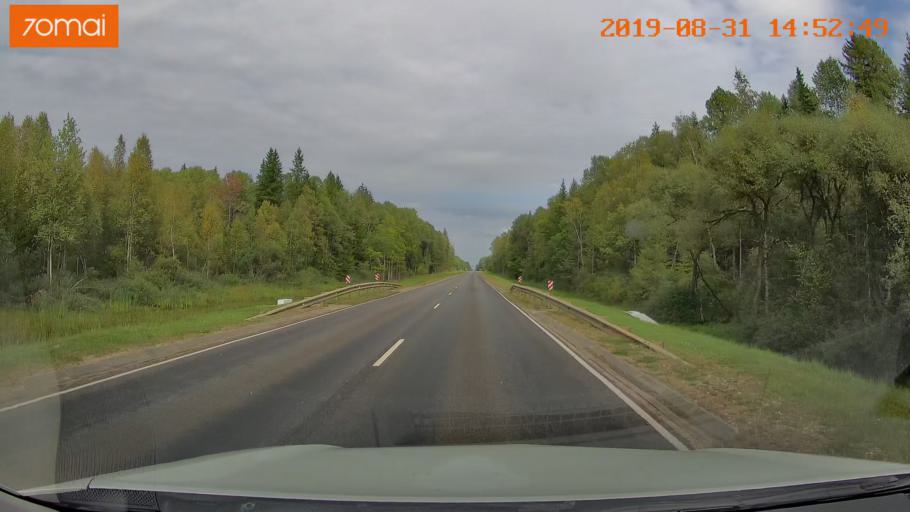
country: RU
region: Kaluga
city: Spas-Demensk
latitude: 54.2787
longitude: 33.8487
